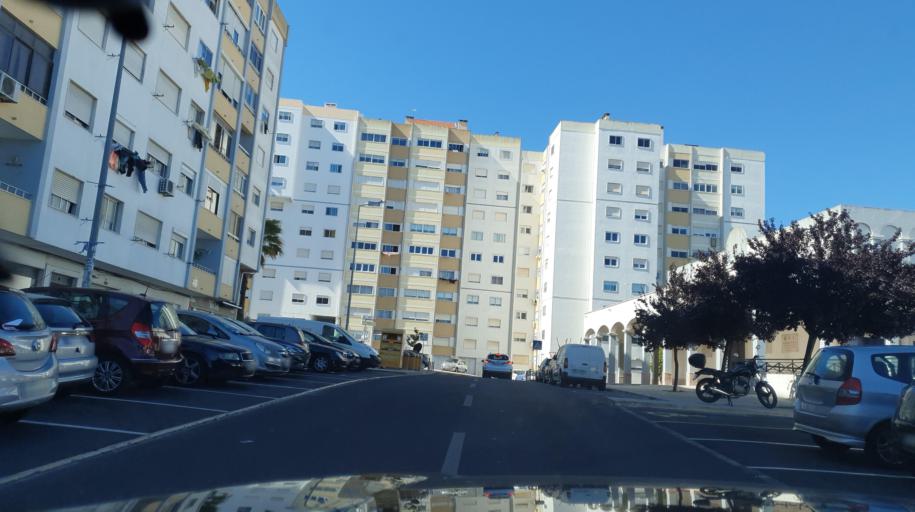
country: PT
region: Lisbon
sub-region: Sintra
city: Cacem
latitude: 38.7537
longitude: -9.2836
